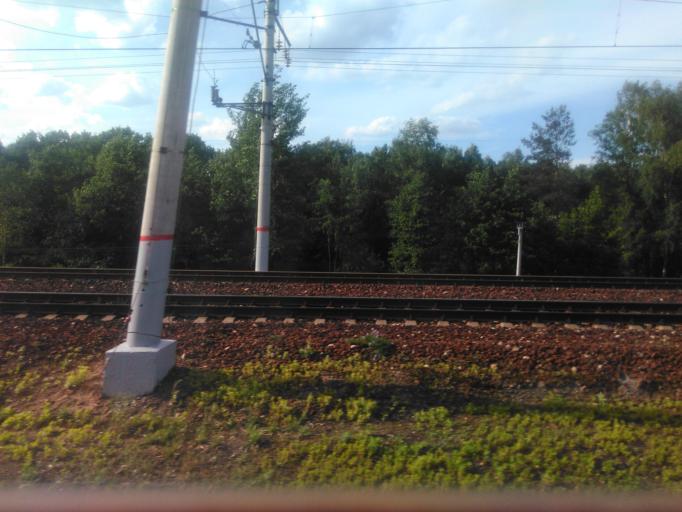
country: RU
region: Moskovskaya
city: Saltykovka
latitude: 55.7516
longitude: 37.9656
